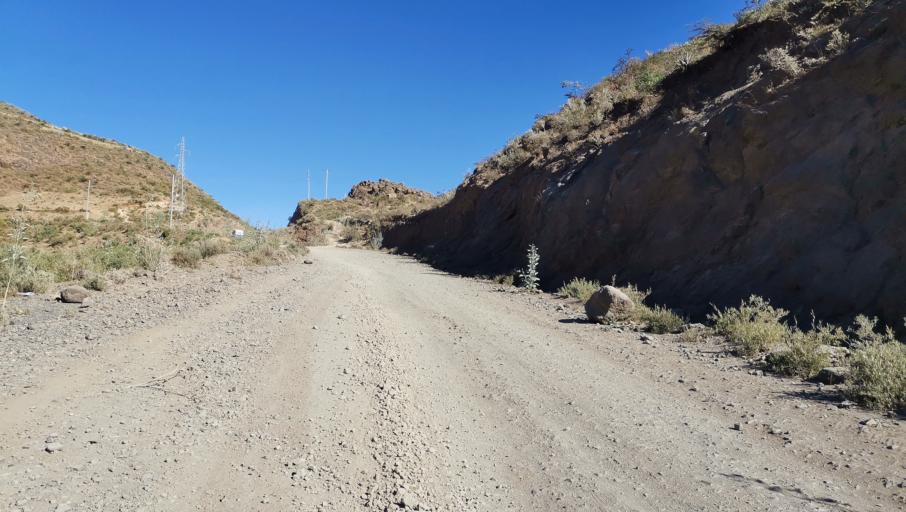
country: ET
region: Tigray
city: Korem
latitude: 12.5891
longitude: 39.0356
